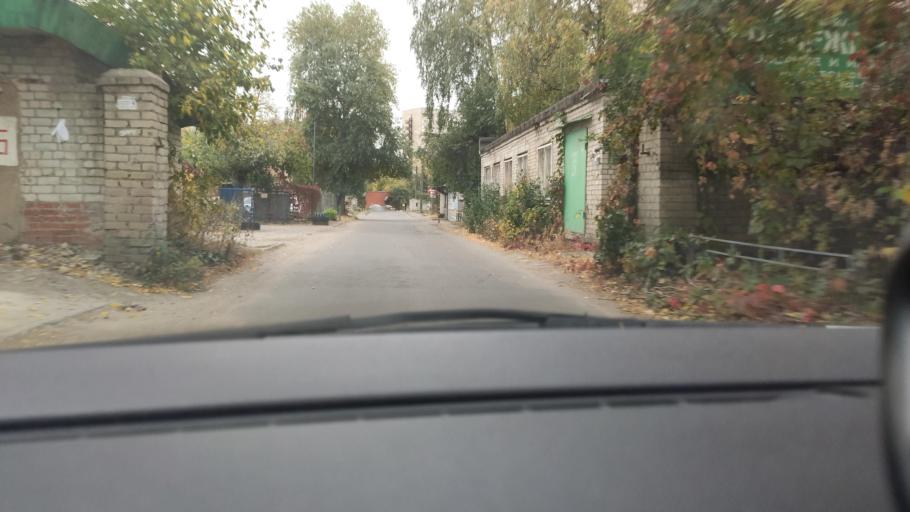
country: RU
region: Voronezj
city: Pridonskoy
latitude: 51.6881
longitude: 39.1243
